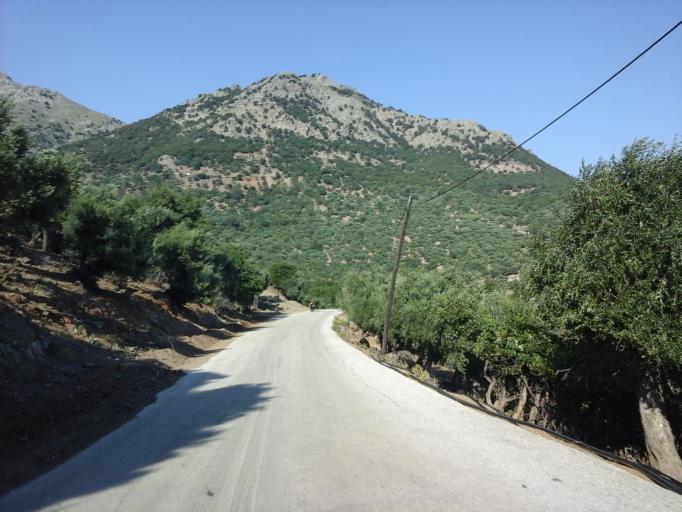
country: GR
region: East Macedonia and Thrace
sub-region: Nomos Evrou
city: Samothraki
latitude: 40.4123
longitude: 25.5569
